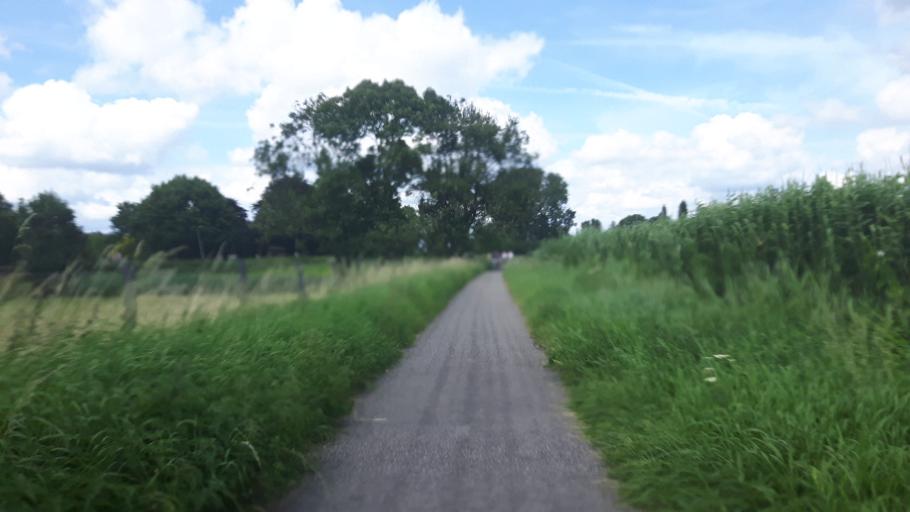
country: NL
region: South Holland
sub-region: Gemeente Vlist
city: Haastrecht
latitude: 52.0117
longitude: 4.7964
